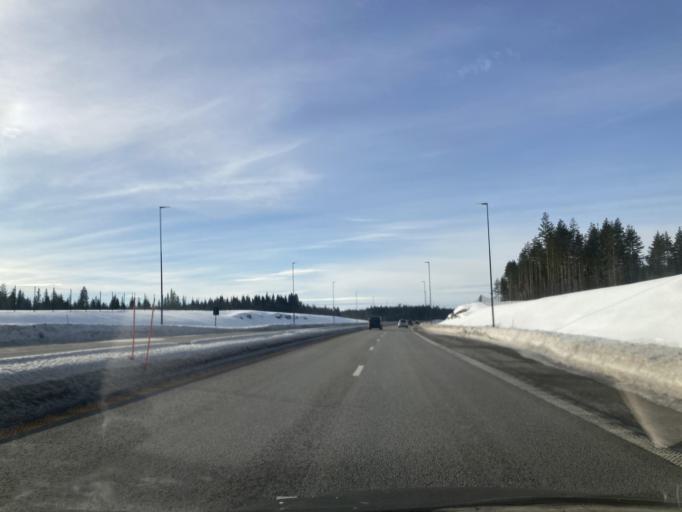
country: NO
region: Hedmark
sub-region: Loten
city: Loten
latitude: 60.8686
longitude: 11.4377
